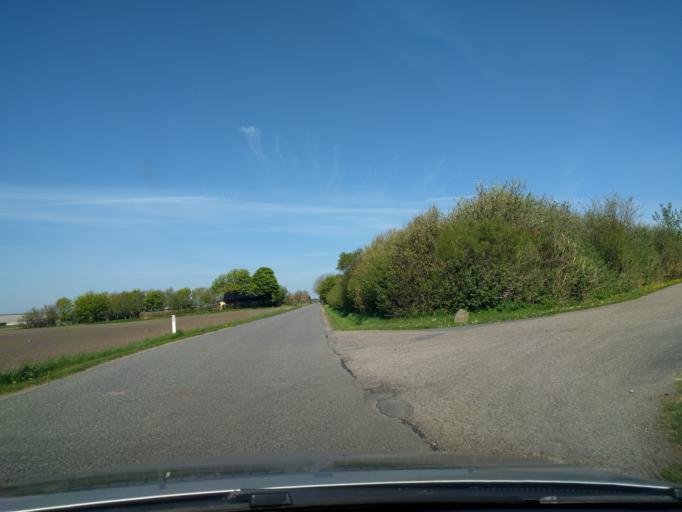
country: DK
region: South Denmark
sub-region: Varde Kommune
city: Olgod
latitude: 55.7864
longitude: 8.6483
